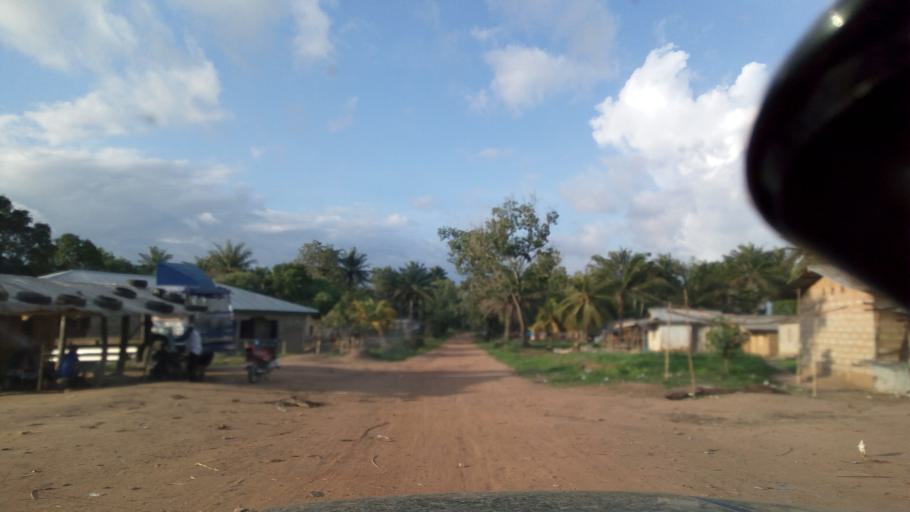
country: SL
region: Northern Province
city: Konakridee
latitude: 8.7774
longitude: -13.1351
